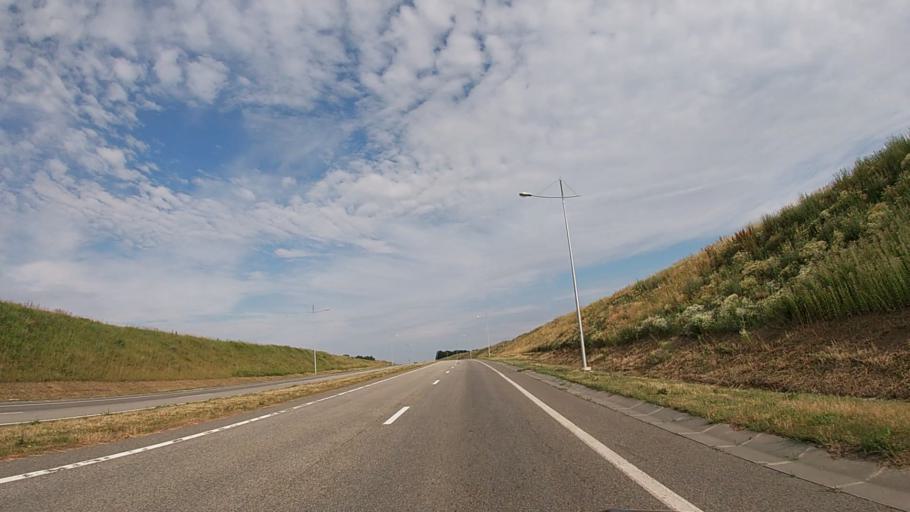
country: RU
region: Belgorod
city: Tomarovka
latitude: 50.7049
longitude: 36.2196
